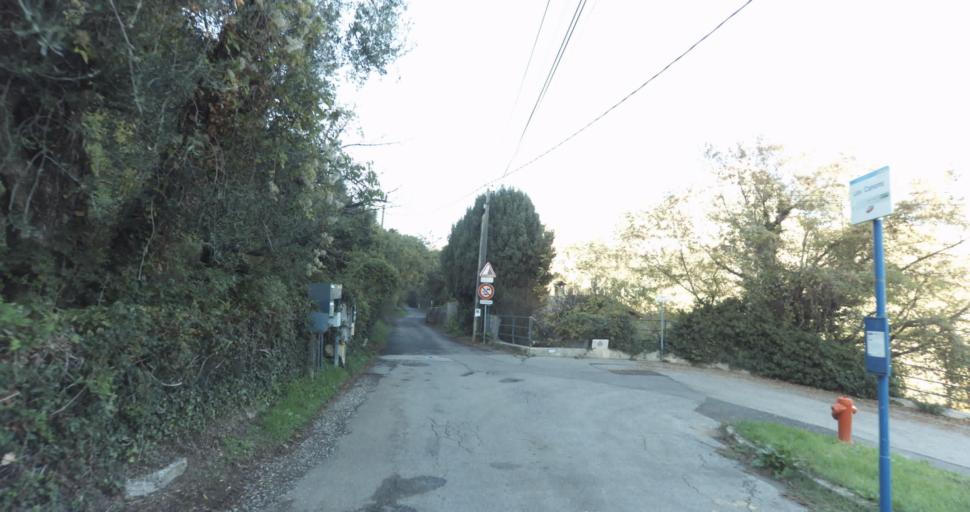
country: FR
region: Provence-Alpes-Cote d'Azur
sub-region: Departement des Alpes-Maritimes
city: Saint-Jeannet
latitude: 43.7416
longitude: 7.1289
